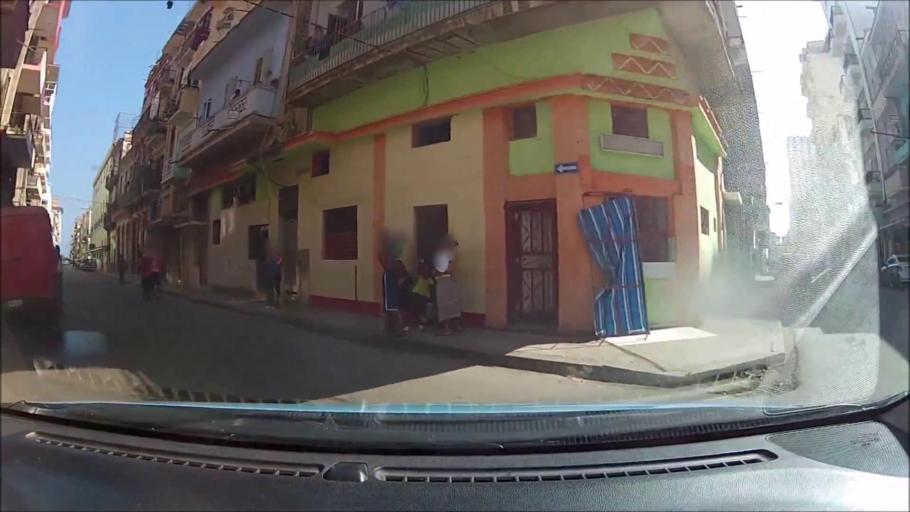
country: CU
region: La Habana
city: Centro Habana
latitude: 23.1382
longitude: -82.3676
